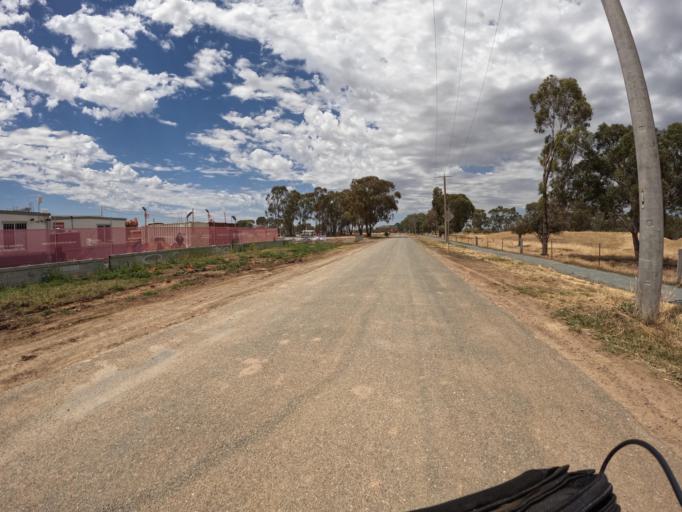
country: AU
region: Victoria
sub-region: Greater Shepparton
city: Shepparton
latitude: -36.6137
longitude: 145.2398
